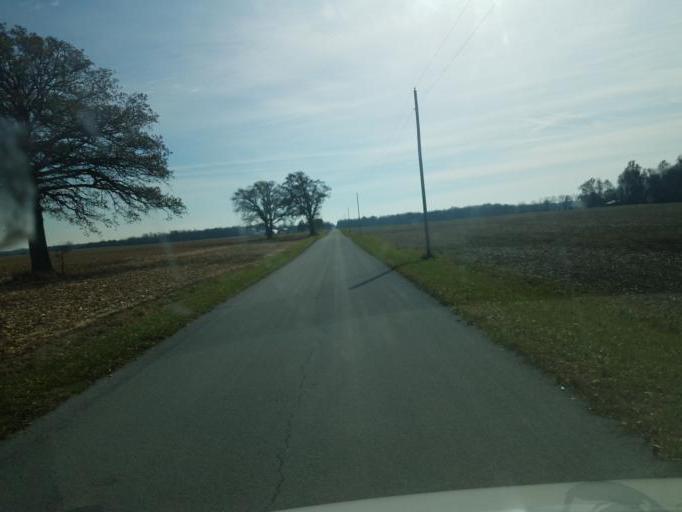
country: US
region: Ohio
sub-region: Hardin County
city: Forest
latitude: 40.6640
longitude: -83.4396
